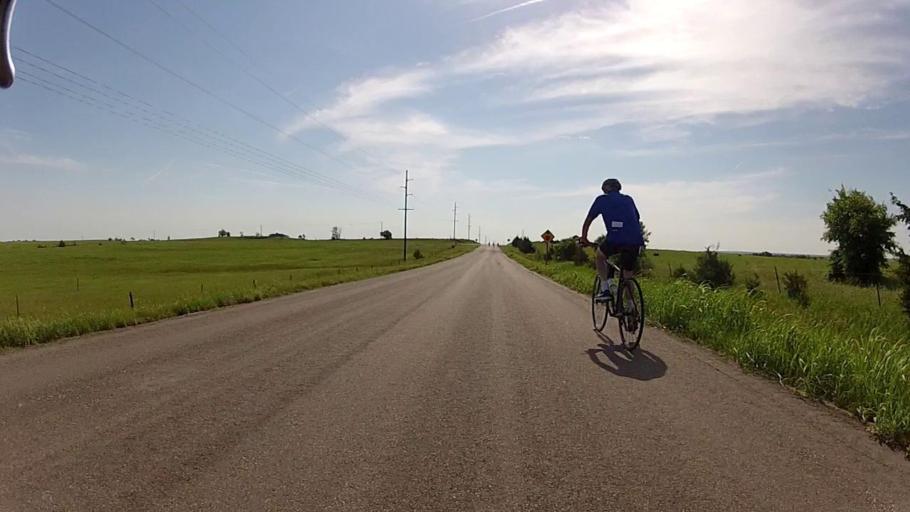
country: US
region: Kansas
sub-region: Cowley County
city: Winfield
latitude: 37.0712
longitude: -96.6460
